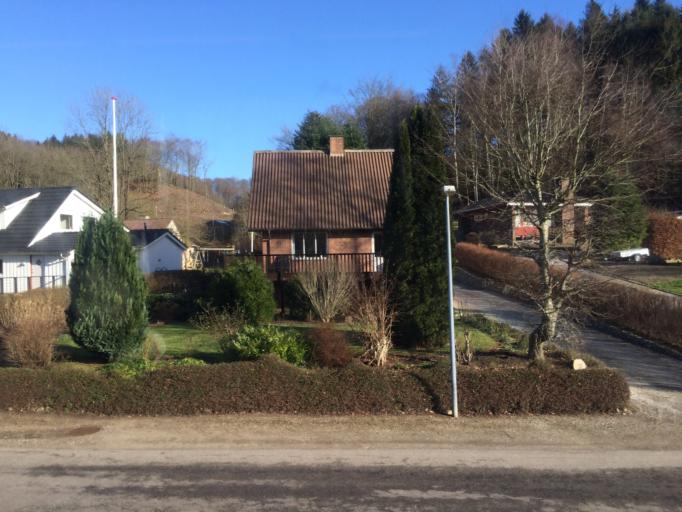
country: DK
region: South Denmark
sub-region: Vejle Kommune
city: Vejle
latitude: 55.7459
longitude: 9.5377
